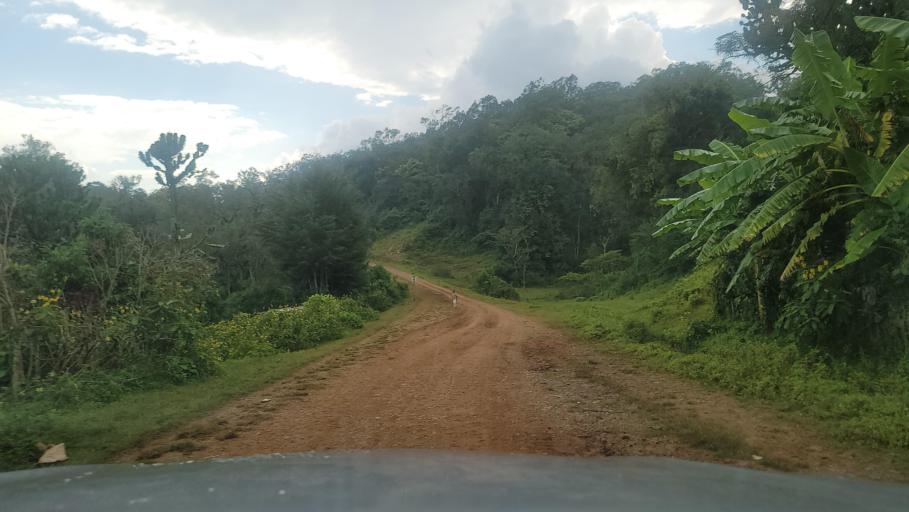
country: ET
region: Southern Nations, Nationalities, and People's Region
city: Bonga
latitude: 7.6307
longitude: 36.2208
